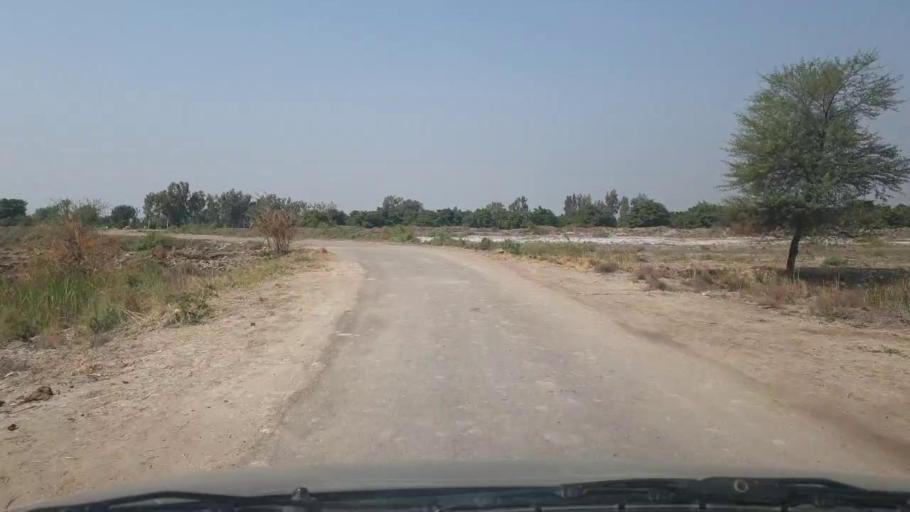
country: PK
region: Sindh
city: Mirwah Gorchani
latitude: 25.3409
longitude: 69.1469
